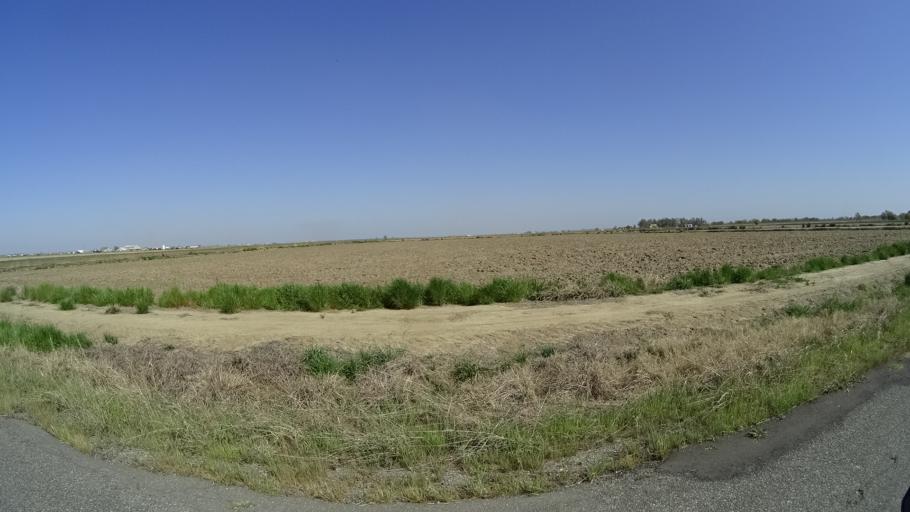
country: US
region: California
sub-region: Glenn County
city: Willows
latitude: 39.4811
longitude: -122.0457
